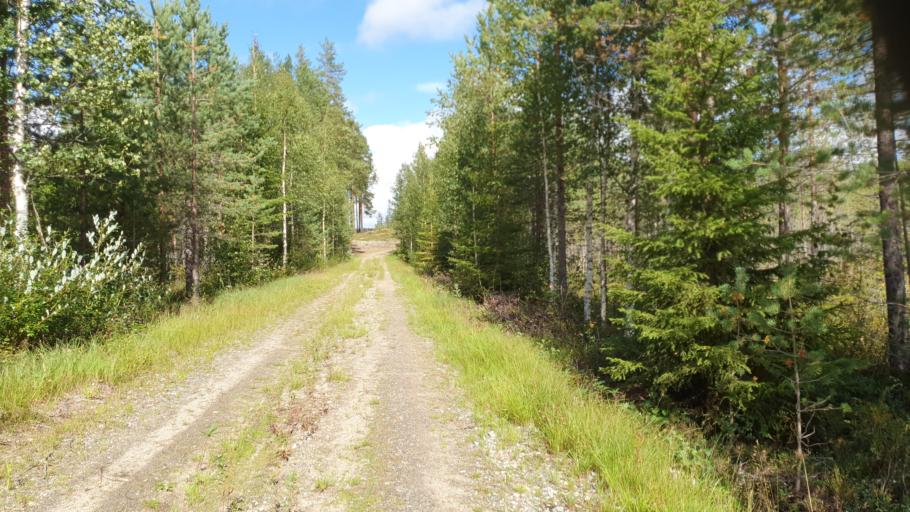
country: FI
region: Kainuu
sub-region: Kehys-Kainuu
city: Kuhmo
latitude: 64.1472
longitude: 29.3555
